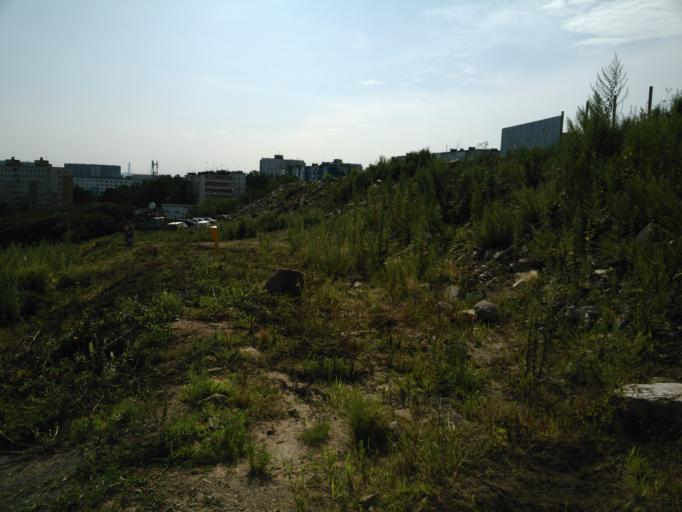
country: RU
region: Primorskiy
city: Vladivostok
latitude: 43.0942
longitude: 131.9824
